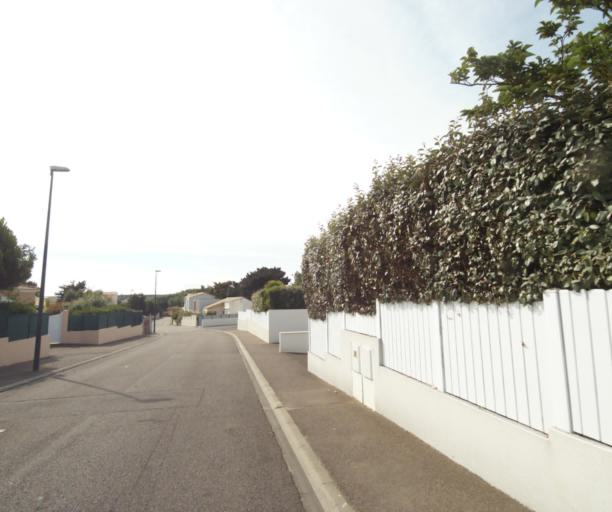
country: FR
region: Pays de la Loire
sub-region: Departement de la Vendee
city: Chateau-d'Olonne
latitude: 46.4820
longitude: -1.7556
